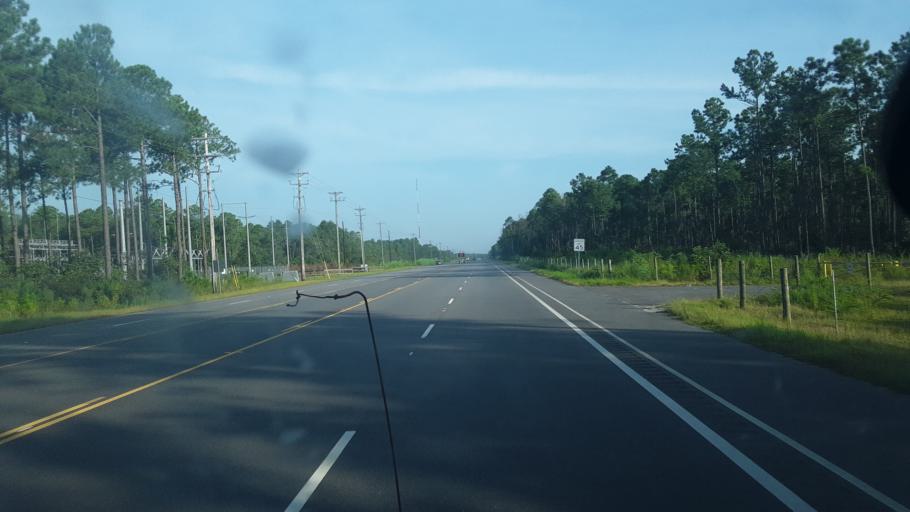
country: US
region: South Carolina
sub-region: Horry County
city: Myrtle Beach
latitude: 33.7721
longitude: -78.8692
